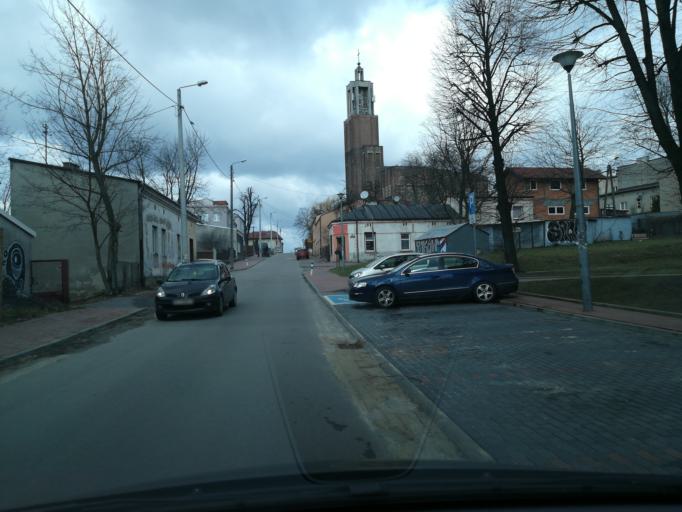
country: PL
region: Silesian Voivodeship
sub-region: Czestochowa
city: Czestochowa
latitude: 50.7910
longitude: 19.1340
